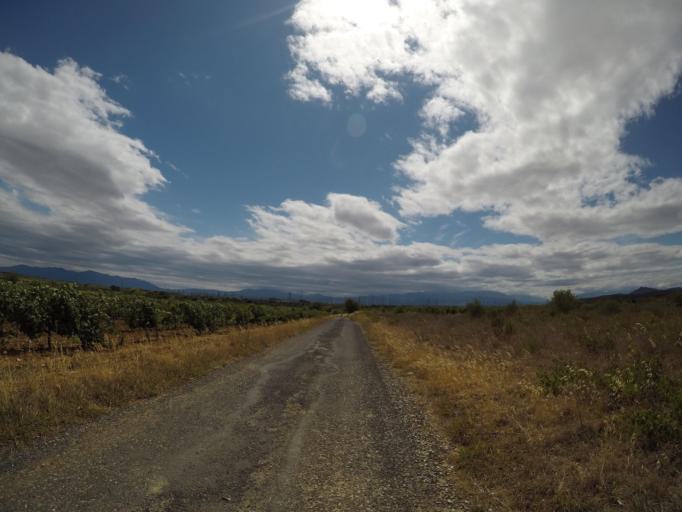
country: FR
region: Languedoc-Roussillon
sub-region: Departement des Pyrenees-Orientales
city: Baixas
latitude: 42.7420
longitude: 2.8053
